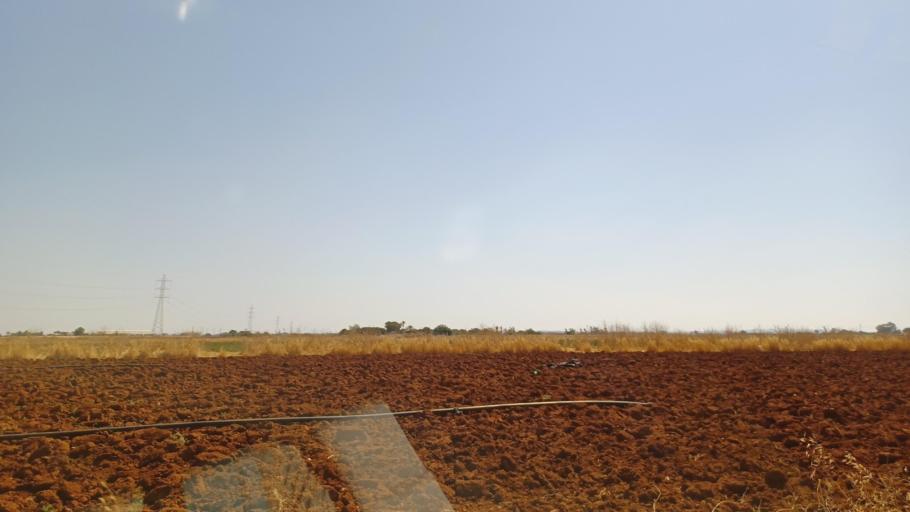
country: CY
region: Ammochostos
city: Avgorou
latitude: 35.0105
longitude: 33.8146
